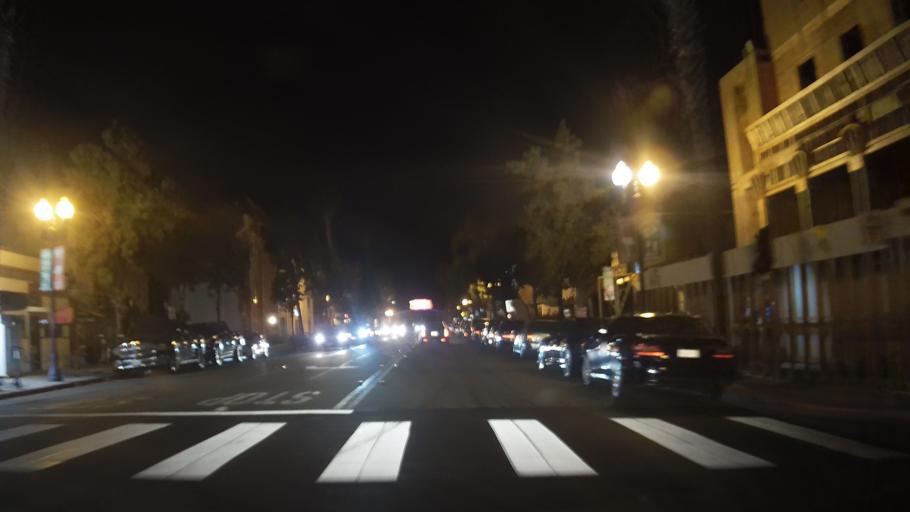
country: US
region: California
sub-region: San Diego County
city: San Diego
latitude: 32.7591
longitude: -117.1463
